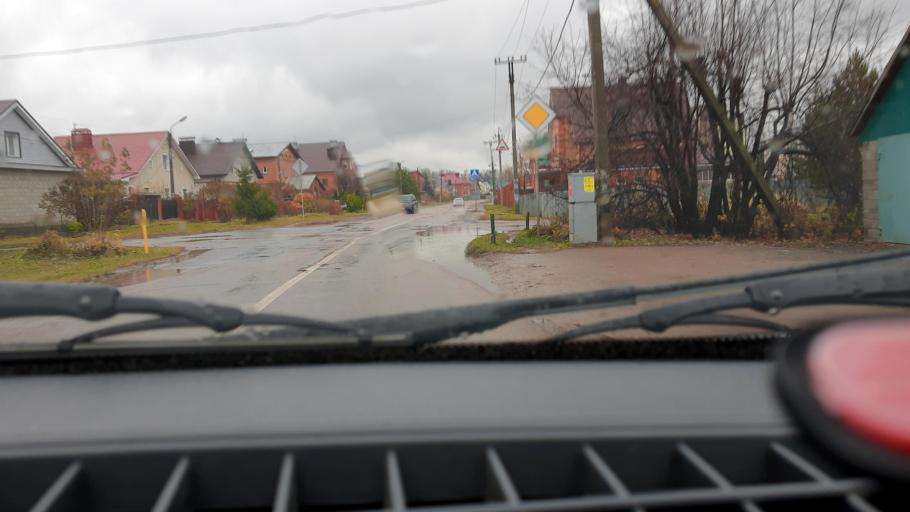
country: RU
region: Bashkortostan
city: Mikhaylovka
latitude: 54.7928
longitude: 55.9451
